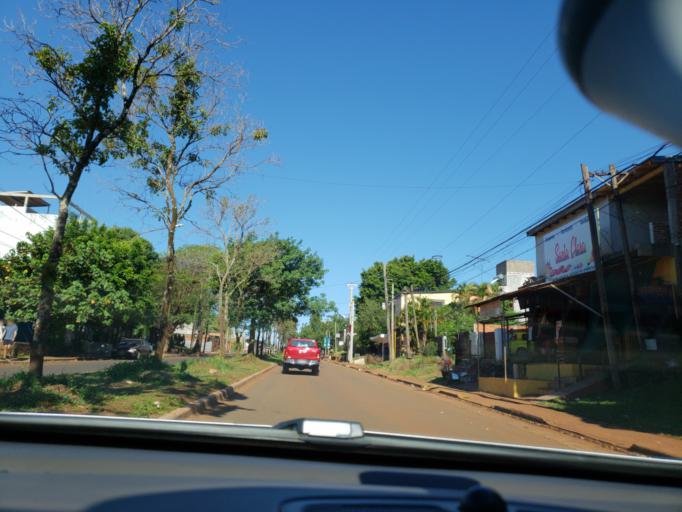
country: AR
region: Misiones
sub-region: Departamento de Capital
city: Posadas
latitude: -27.3853
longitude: -55.9219
